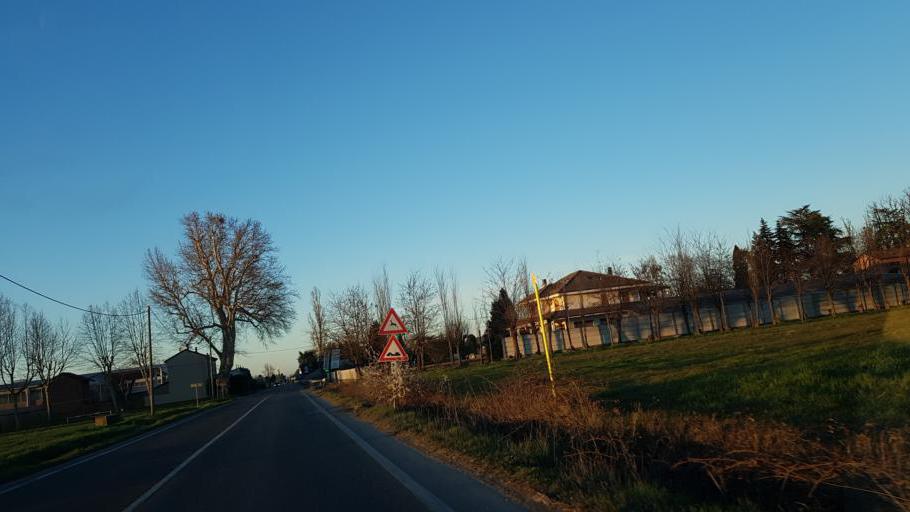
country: IT
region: Piedmont
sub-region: Provincia di Alessandria
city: Carbonara Scrivia
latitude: 44.8624
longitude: 8.8556
